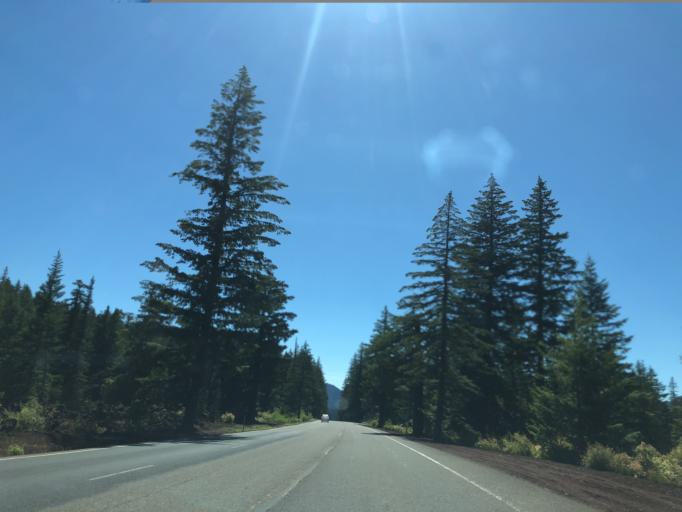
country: US
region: Oregon
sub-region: Deschutes County
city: Sisters
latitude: 44.4321
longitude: -121.9712
